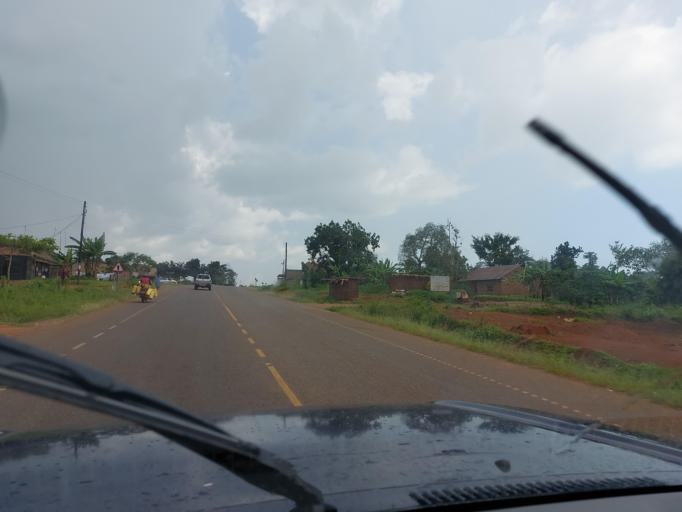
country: UG
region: Central Region
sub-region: Buikwe District
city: Buikwe
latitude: 0.2411
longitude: 32.9363
